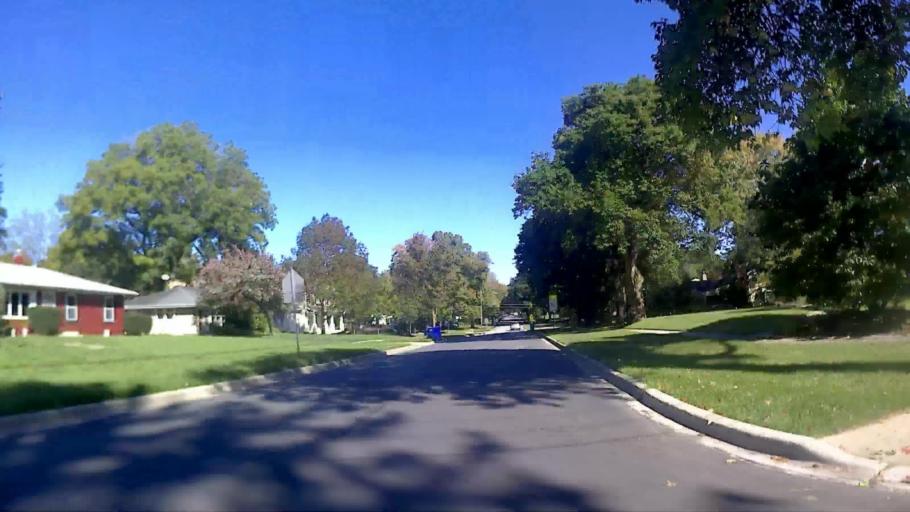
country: US
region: Illinois
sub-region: DuPage County
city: Glen Ellyn
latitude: 41.8633
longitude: -88.0822
